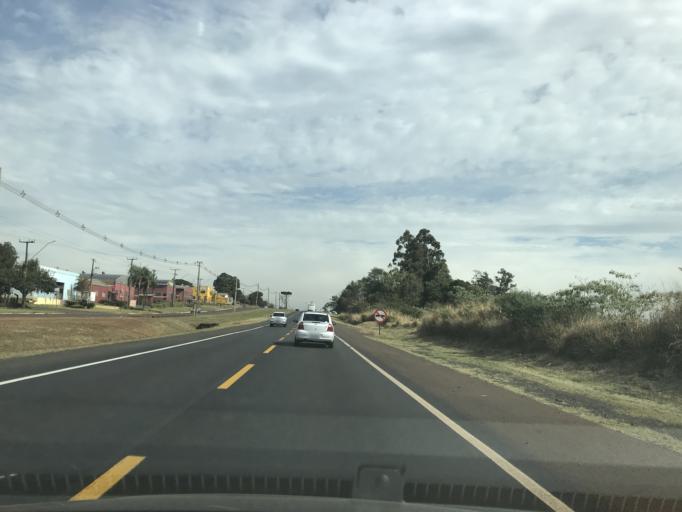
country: BR
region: Parana
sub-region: Cascavel
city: Cascavel
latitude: -25.0413
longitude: -53.6020
